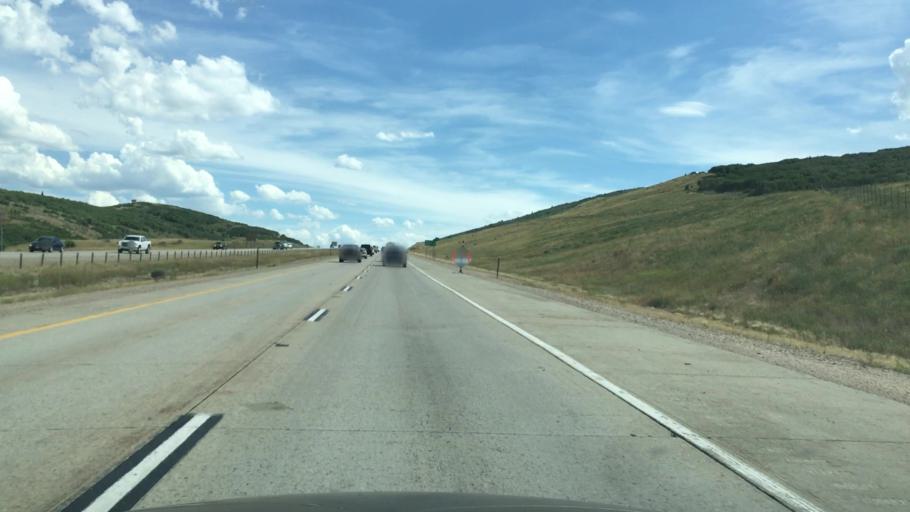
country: US
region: Utah
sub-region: Summit County
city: Park City
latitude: 40.6662
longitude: -111.4594
